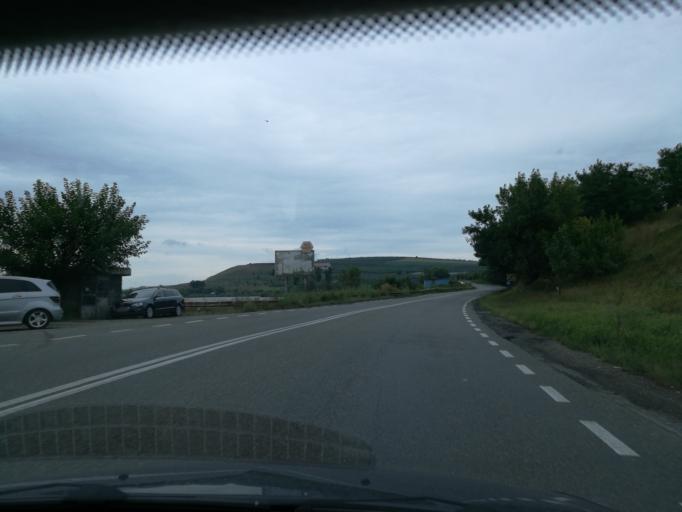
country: RO
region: Suceava
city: Bunesti-Regat
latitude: 47.4844
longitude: 26.2916
